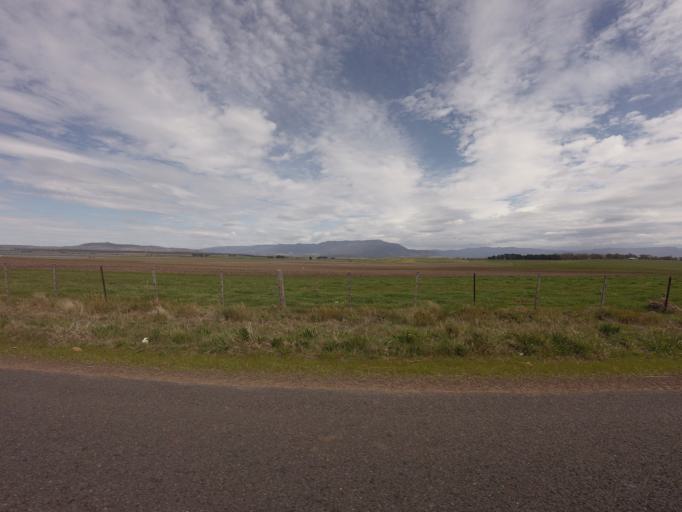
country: AU
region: Tasmania
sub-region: Northern Midlands
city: Evandale
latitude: -41.8050
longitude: 147.2743
